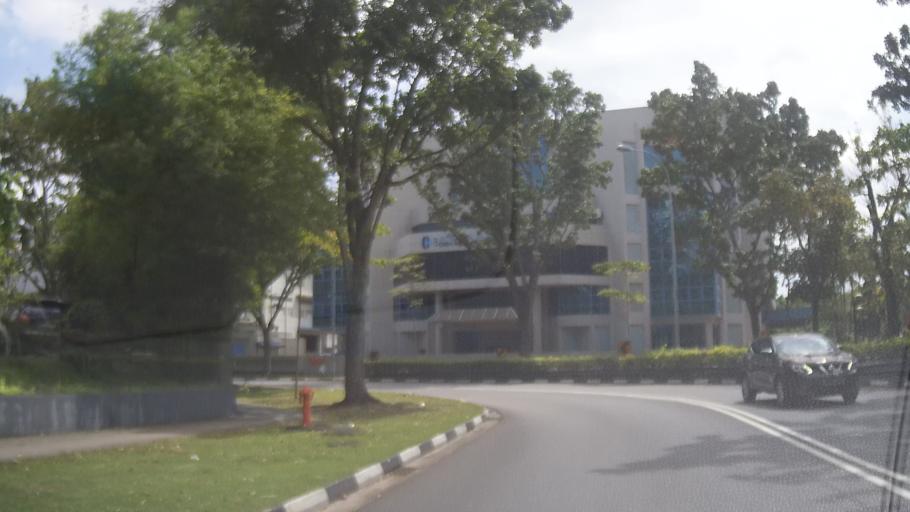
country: MY
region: Johor
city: Johor Bahru
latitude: 1.4087
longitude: 103.7434
